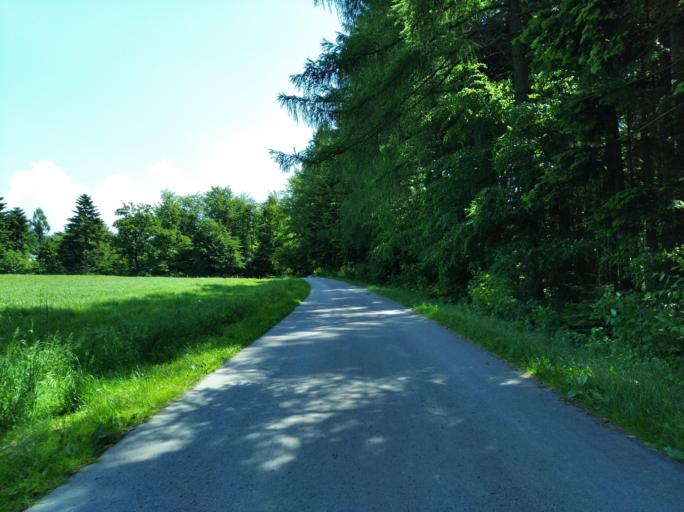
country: PL
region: Subcarpathian Voivodeship
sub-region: Powiat ropczycko-sedziszowski
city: Wielopole Skrzynskie
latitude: 49.9841
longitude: 21.6155
